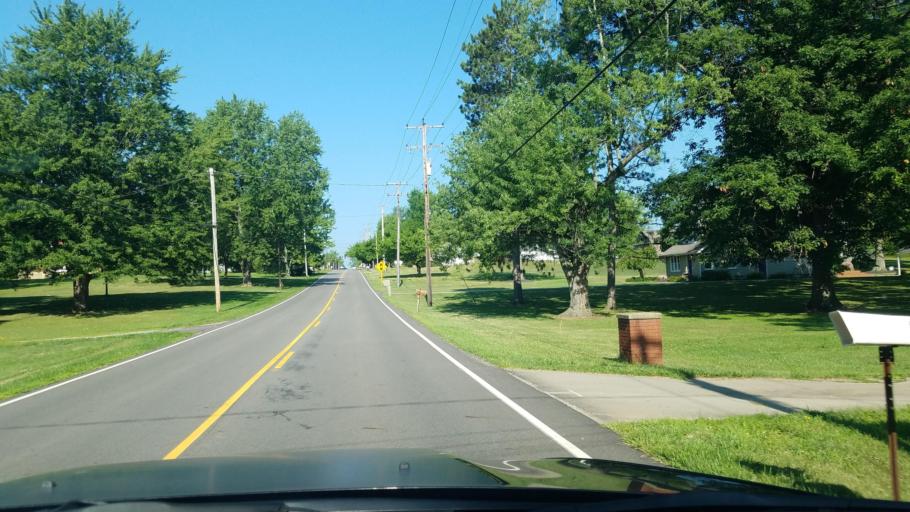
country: US
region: Ohio
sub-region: Trumbull County
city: Champion Heights
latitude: 41.2916
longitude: -80.8441
